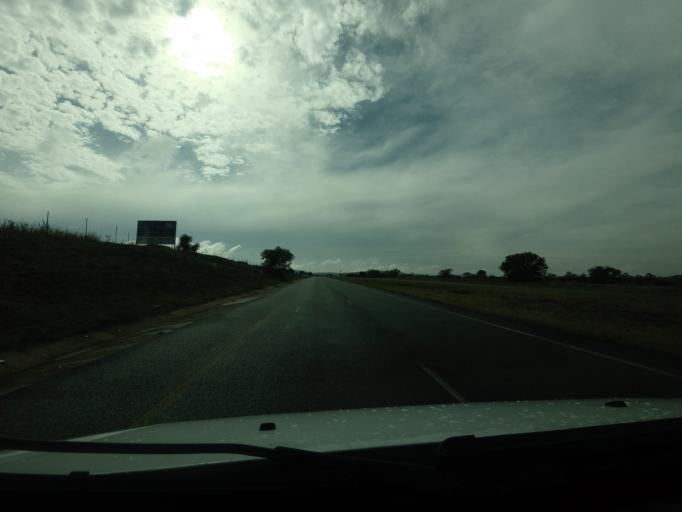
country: ZA
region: Gauteng
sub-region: City of Tshwane Metropolitan Municipality
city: Cullinan
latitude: -25.7719
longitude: 28.4254
